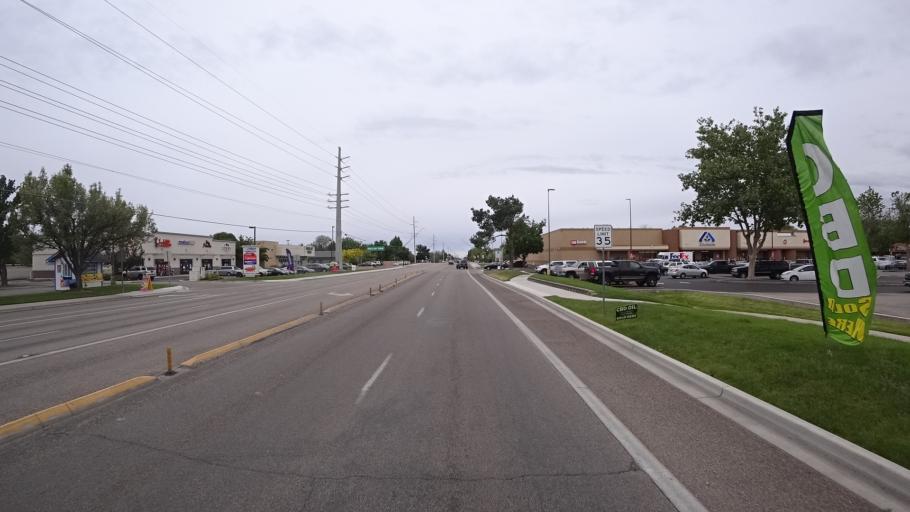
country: US
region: Idaho
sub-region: Ada County
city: Eagle
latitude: 43.6340
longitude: -116.3149
